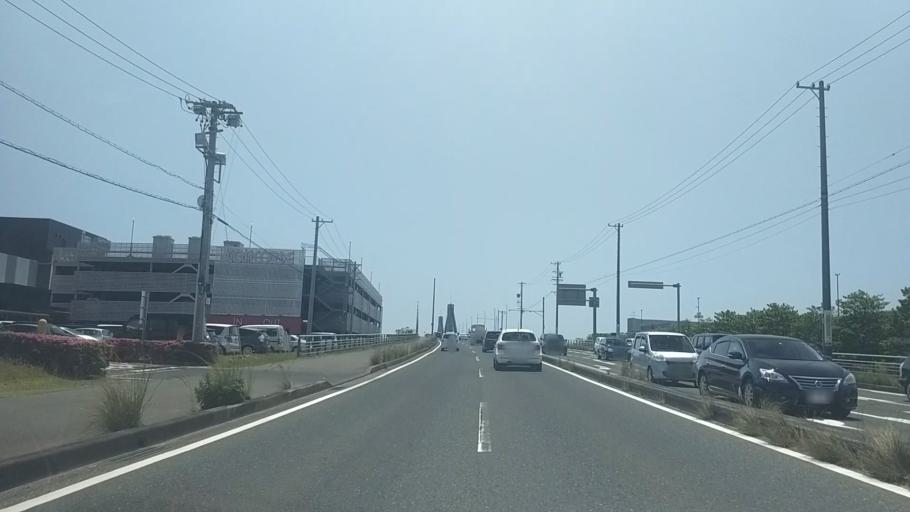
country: JP
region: Shizuoka
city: Hamamatsu
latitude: 34.6953
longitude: 137.6478
